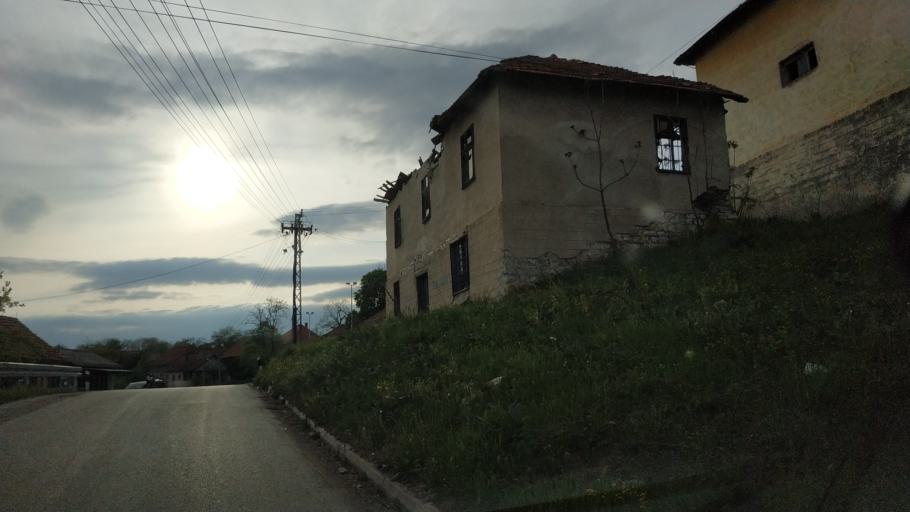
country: RS
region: Central Serbia
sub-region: Zajecarski Okrug
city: Soko Banja
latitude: 43.5280
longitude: 21.8545
